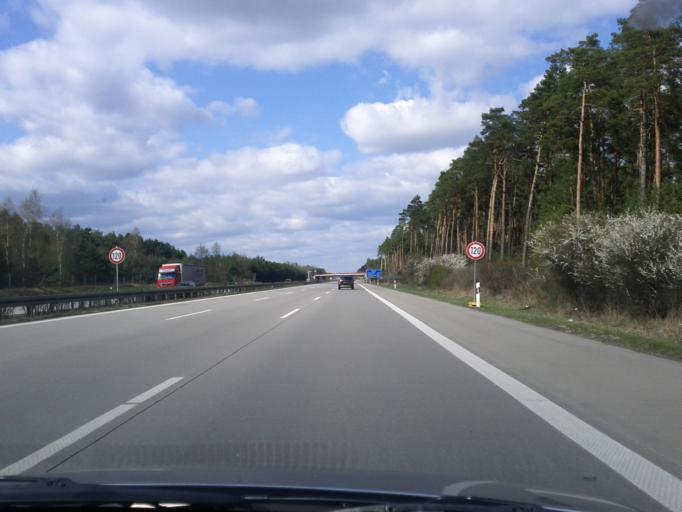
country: DE
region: Brandenburg
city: Grunheide
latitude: 52.3944
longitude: 13.7867
